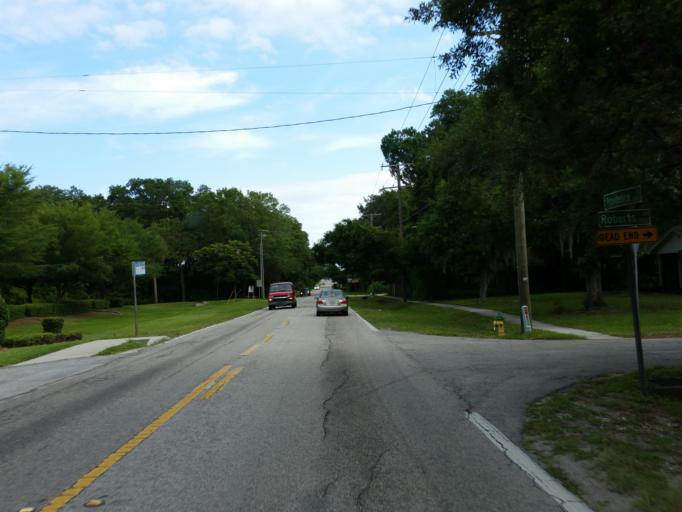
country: US
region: Florida
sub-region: Hillsborough County
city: Riverview
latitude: 27.8817
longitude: -82.3184
